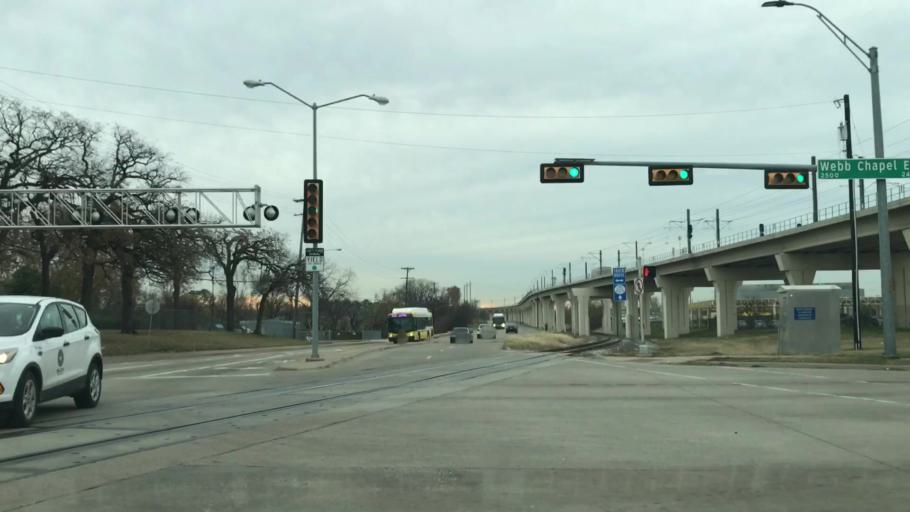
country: US
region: Texas
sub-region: Dallas County
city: University Park
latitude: 32.8522
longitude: -96.8763
